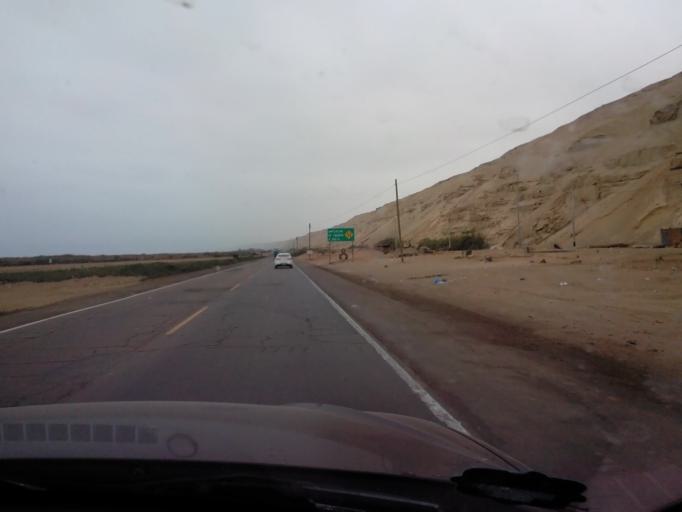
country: PE
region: Ica
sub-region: Provincia de Chincha
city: Sunampe
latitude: -13.4087
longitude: -76.1912
